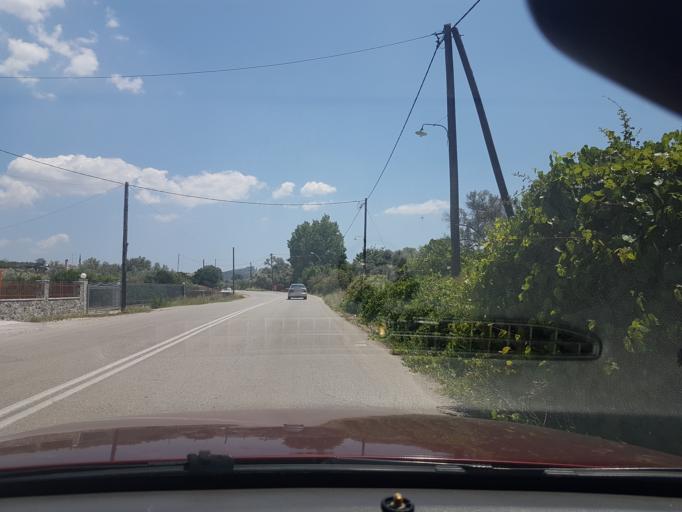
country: GR
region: Central Greece
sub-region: Nomos Evvoias
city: Mytikas
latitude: 38.4575
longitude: 23.6556
